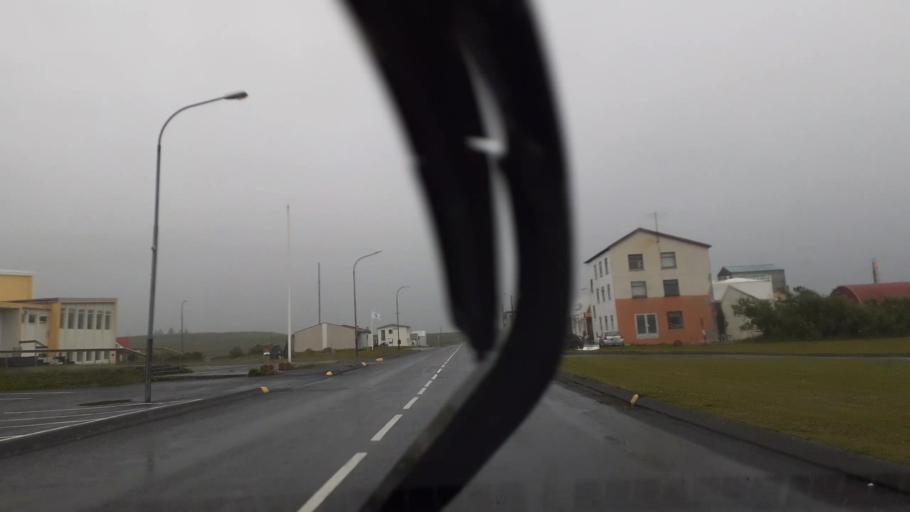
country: IS
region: Northeast
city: Husavik
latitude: 66.4533
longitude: -15.9501
